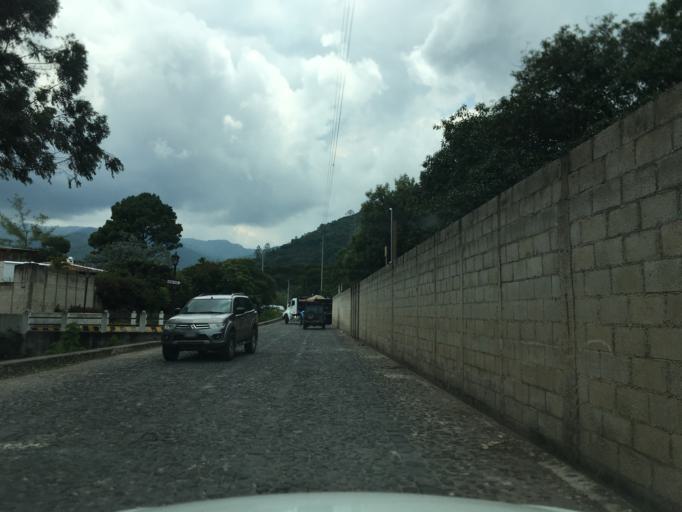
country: GT
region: Sacatepequez
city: Antigua Guatemala
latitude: 14.5478
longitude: -90.7311
